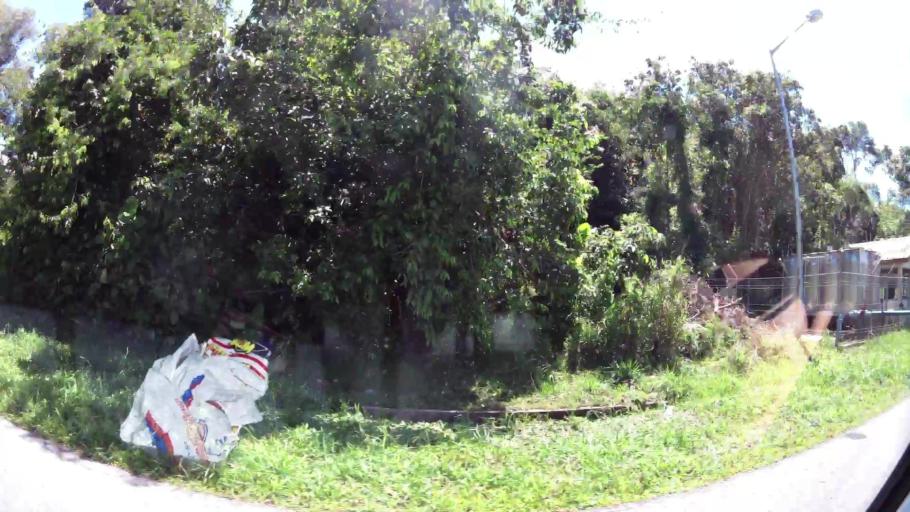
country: BN
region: Brunei and Muara
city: Bandar Seri Begawan
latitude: 5.0315
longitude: 115.0594
